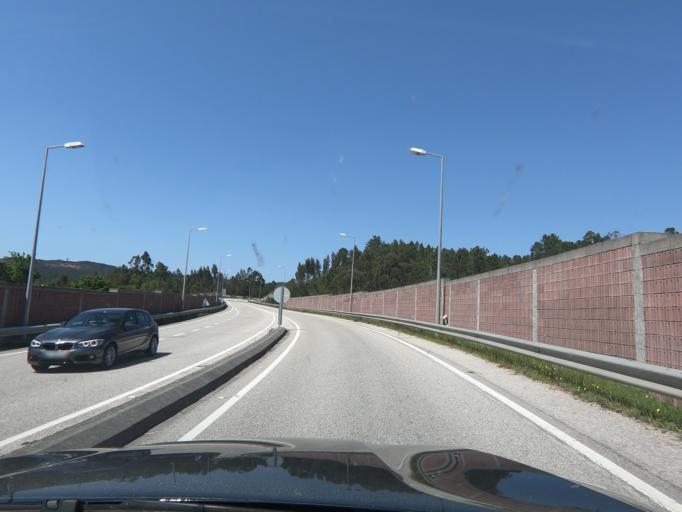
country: PT
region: Coimbra
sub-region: Miranda do Corvo
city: Miranda do Corvo
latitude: 40.0921
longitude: -8.3155
